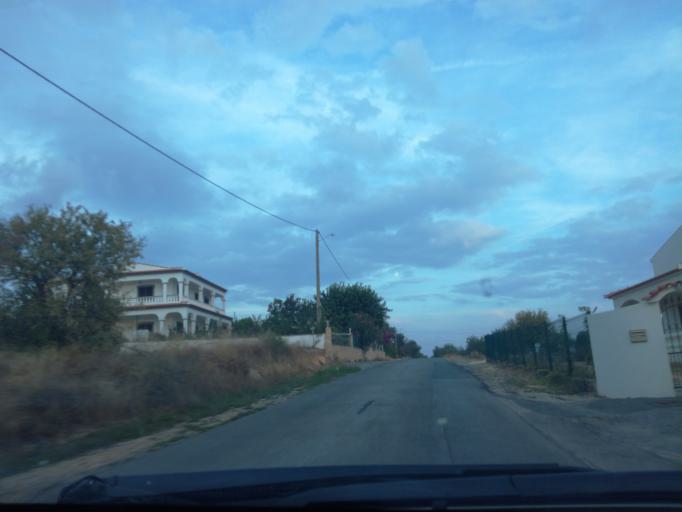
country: PT
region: Faro
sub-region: Olhao
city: Olhao
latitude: 37.0834
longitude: -7.8684
